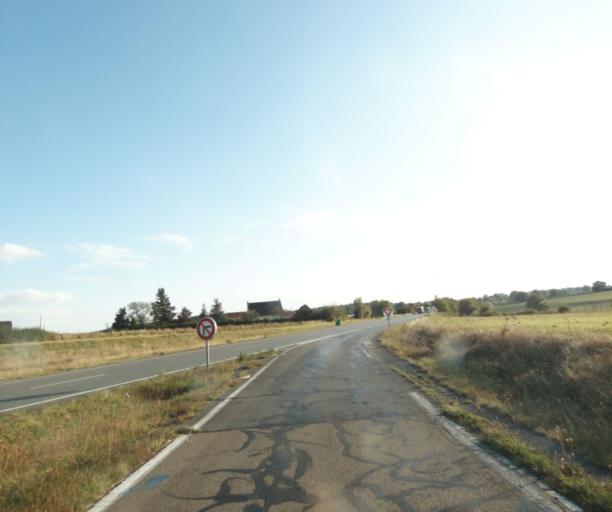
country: FR
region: Bourgogne
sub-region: Departement de Saone-et-Loire
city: Palinges
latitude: 46.5594
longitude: 4.1869
